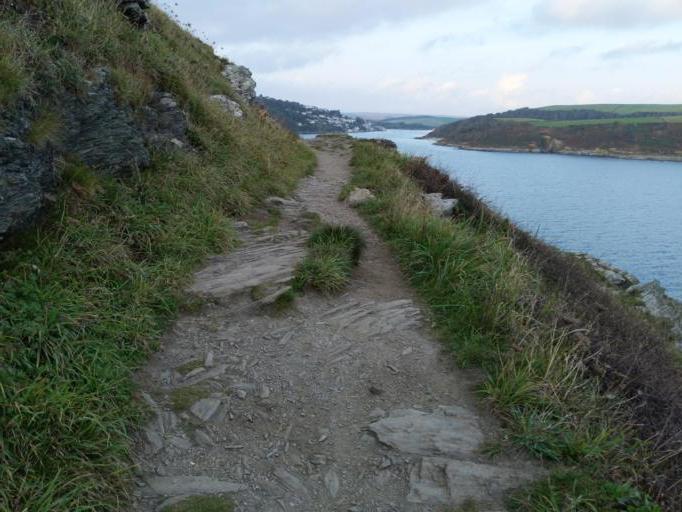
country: GB
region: England
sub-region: Devon
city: Salcombe
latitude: 50.2163
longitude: -3.7823
